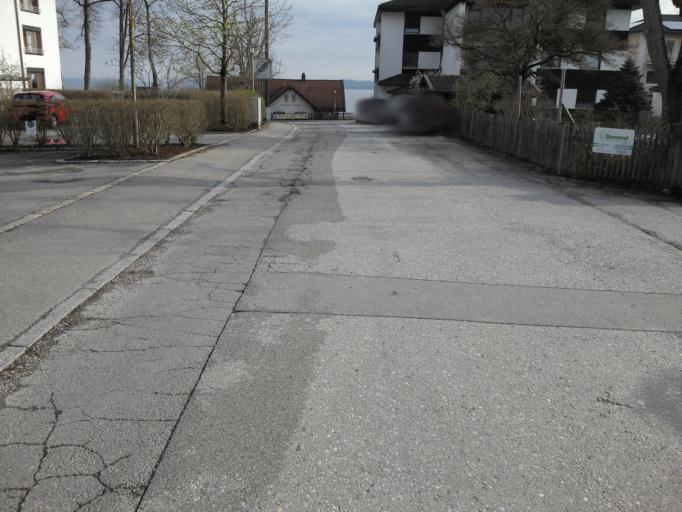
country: DE
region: Bavaria
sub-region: Upper Bavaria
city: Seeshaupt
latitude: 47.8235
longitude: 11.3050
